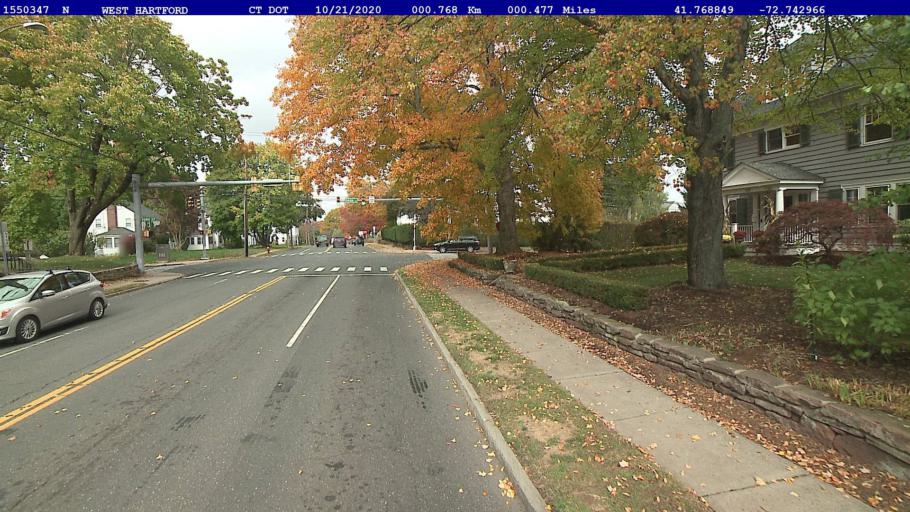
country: US
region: Connecticut
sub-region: Hartford County
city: West Hartford
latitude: 41.7689
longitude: -72.7430
